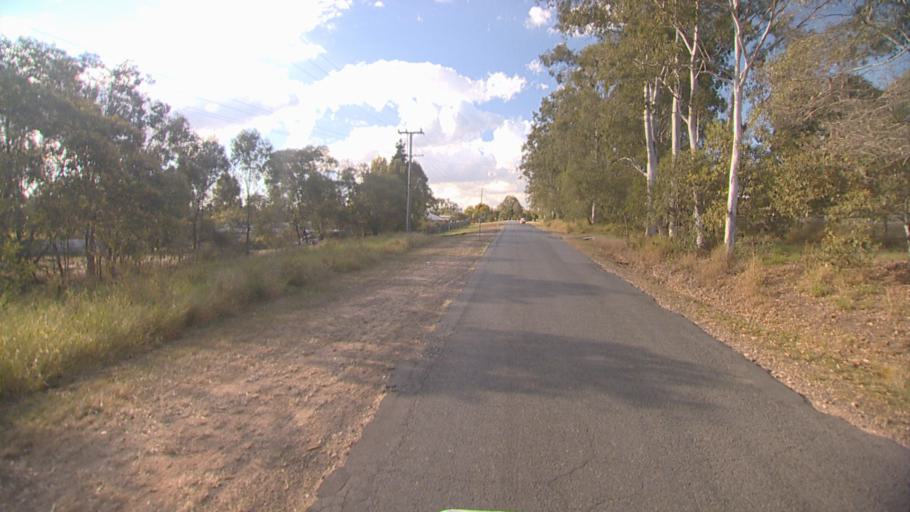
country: AU
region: Queensland
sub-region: Ipswich
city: Springfield Lakes
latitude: -27.7371
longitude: 152.9440
